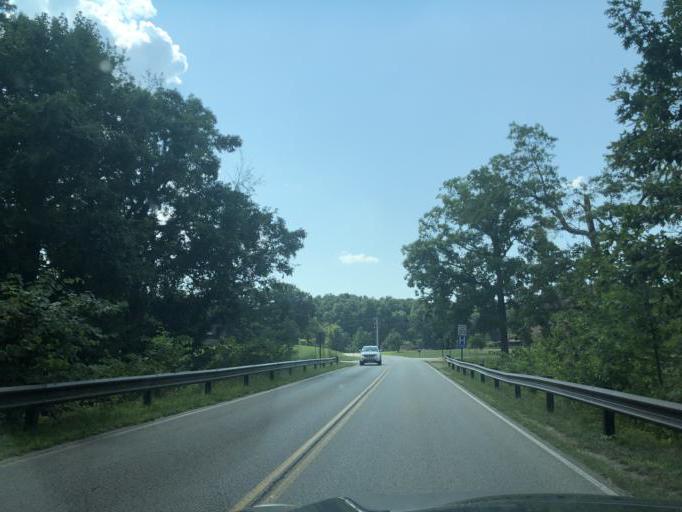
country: US
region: Tennessee
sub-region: Franklin County
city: Sewanee
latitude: 35.2085
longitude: -85.9125
